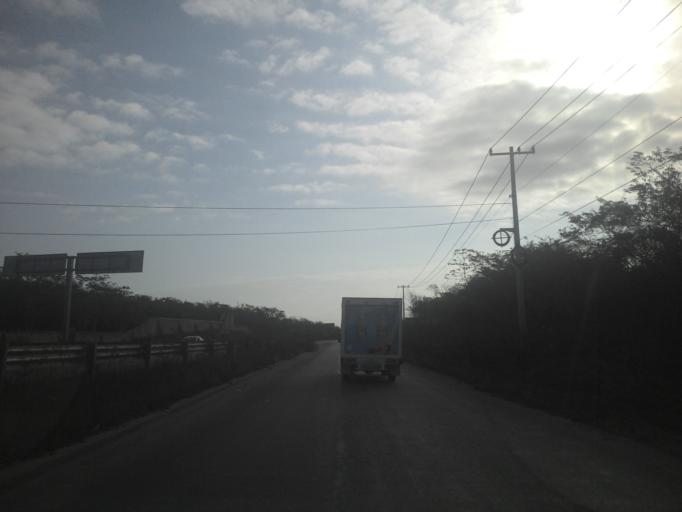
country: MX
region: Yucatan
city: Valladolid
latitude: 20.7250
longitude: -88.1997
